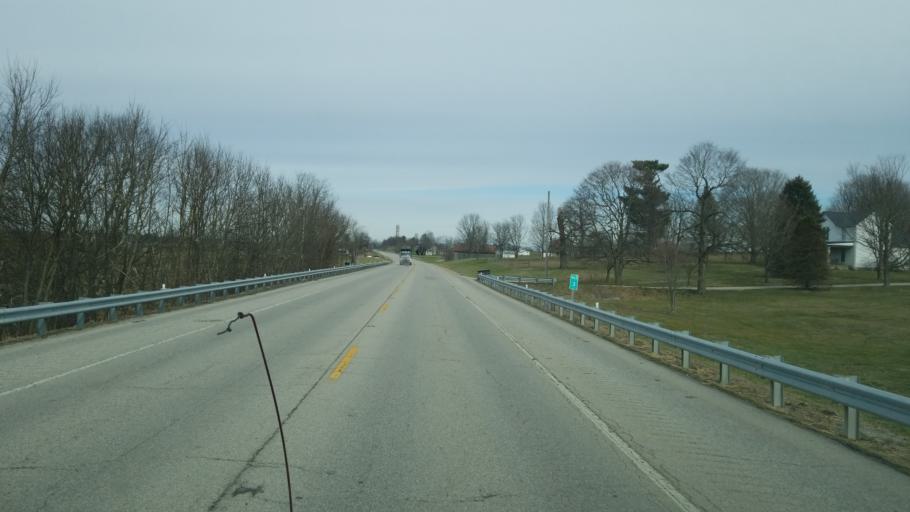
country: US
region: Kentucky
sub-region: Fleming County
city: Flemingsburg
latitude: 38.4952
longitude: -83.8545
